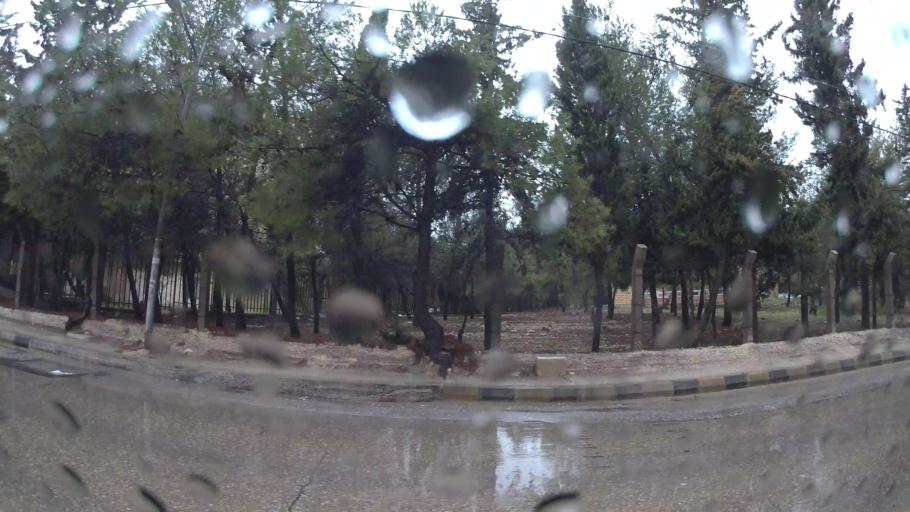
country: JO
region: Amman
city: Al Jubayhah
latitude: 32.0194
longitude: 35.8755
